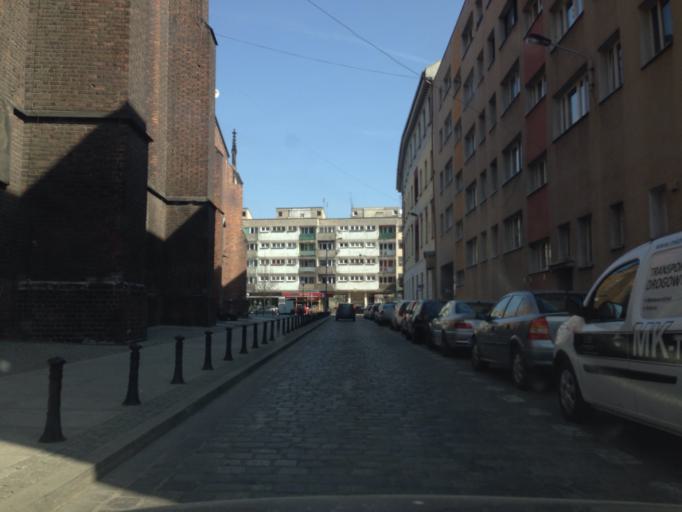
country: PL
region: Lower Silesian Voivodeship
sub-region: Powiat wroclawski
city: Wroclaw
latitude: 51.1093
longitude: 17.0355
